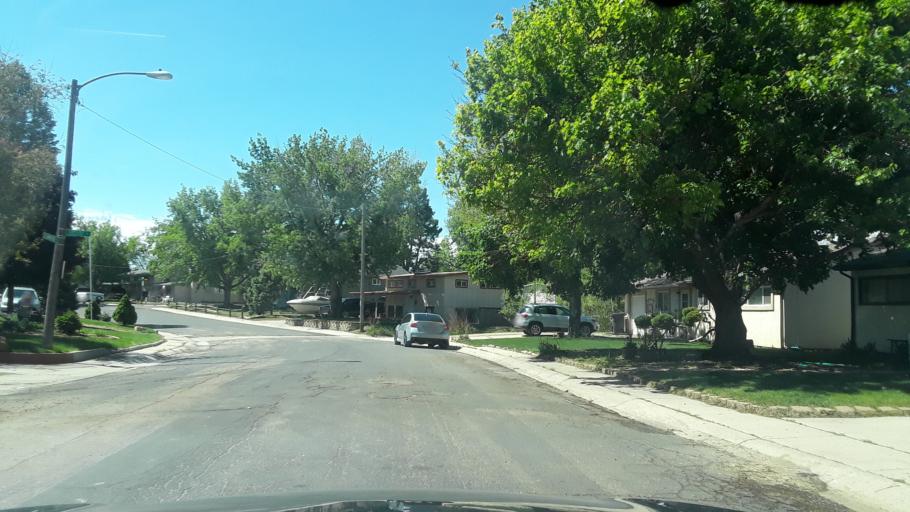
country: US
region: Colorado
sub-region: El Paso County
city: Colorado Springs
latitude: 38.8951
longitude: -104.8169
